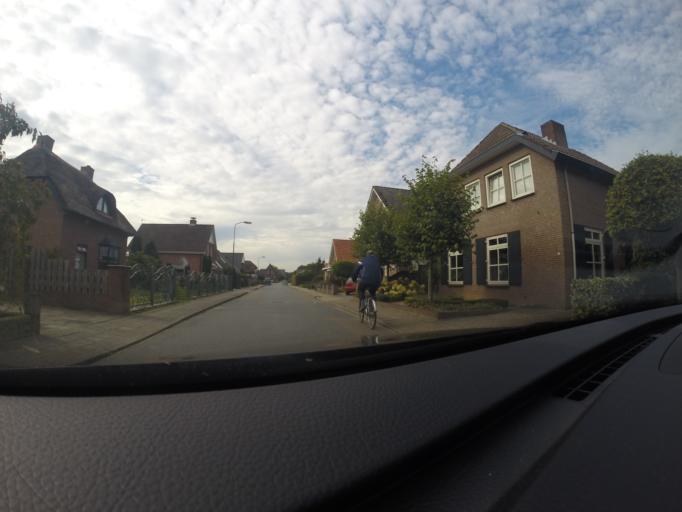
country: NL
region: Gelderland
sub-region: Gemeente Doetinchem
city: Doetinchem
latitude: 51.9624
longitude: 6.2140
